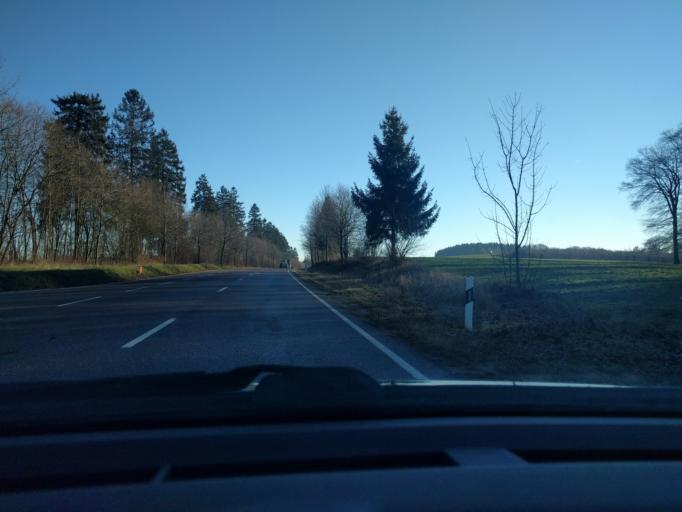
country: LU
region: Diekirch
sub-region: Canton de Clervaux
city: Weiswampach
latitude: 50.1602
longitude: 6.0324
